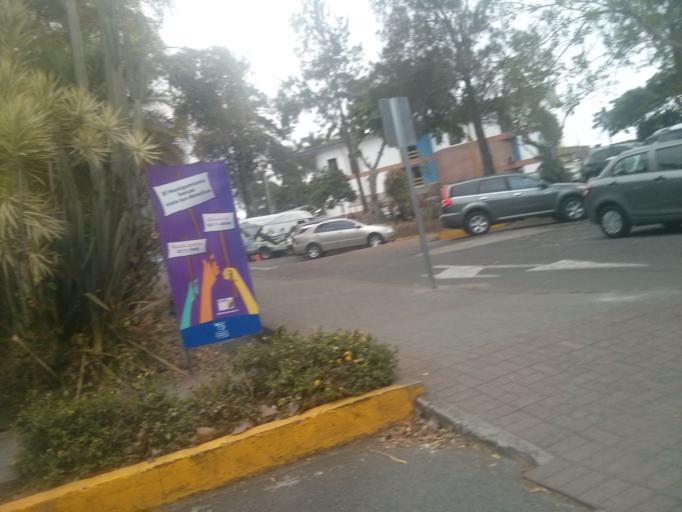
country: CR
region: San Jose
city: San Pedro
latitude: 9.9351
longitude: -84.0539
